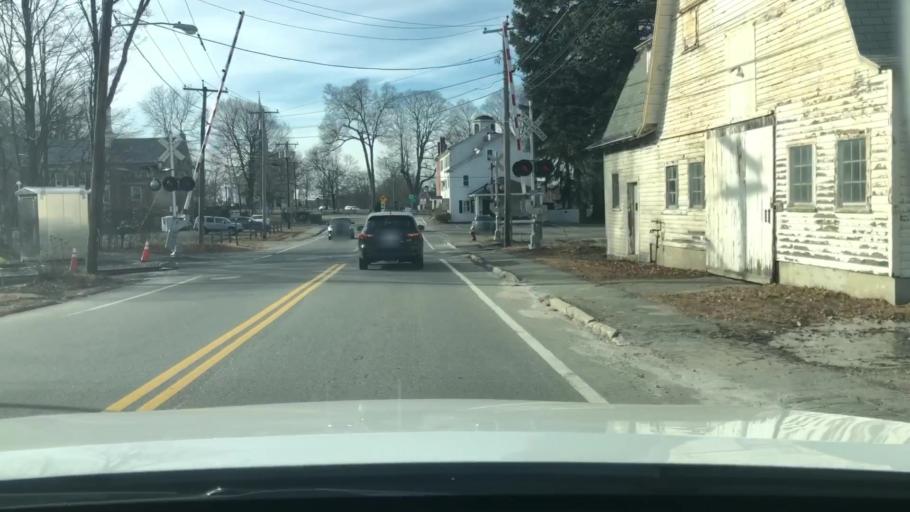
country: US
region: Massachusetts
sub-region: Worcester County
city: Grafton
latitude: 42.2065
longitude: -71.6833
